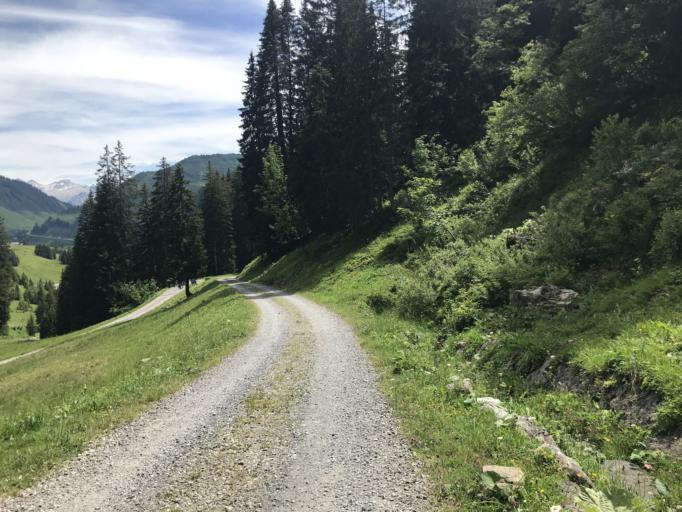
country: AT
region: Vorarlberg
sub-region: Politischer Bezirk Bregenz
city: Damuels
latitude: 47.2975
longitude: 9.8726
